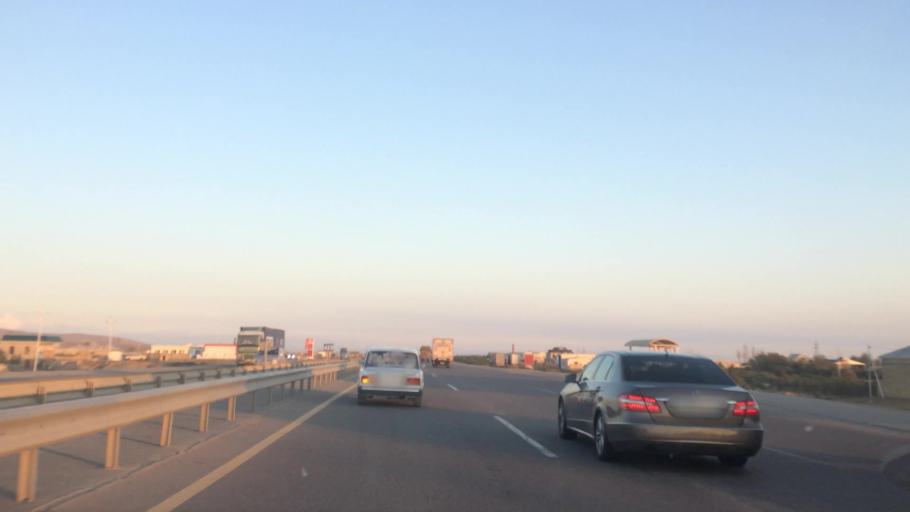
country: AZ
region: Baki
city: Qobustan
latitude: 39.9695
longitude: 49.2670
